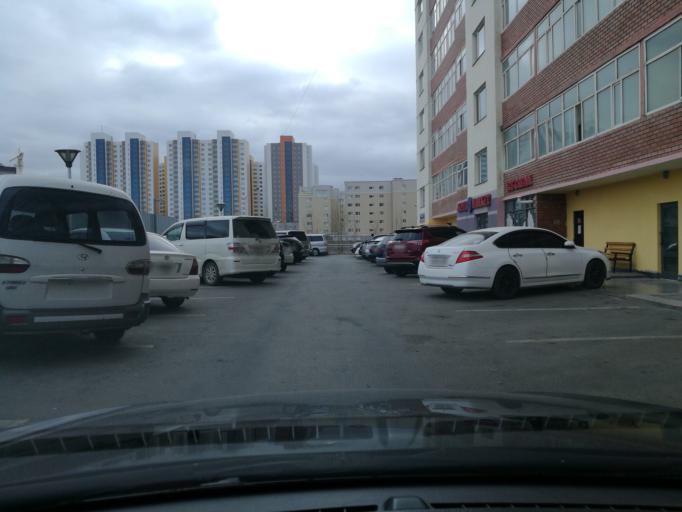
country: MN
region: Ulaanbaatar
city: Ulaanbaatar
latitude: 47.9004
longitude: 106.9207
